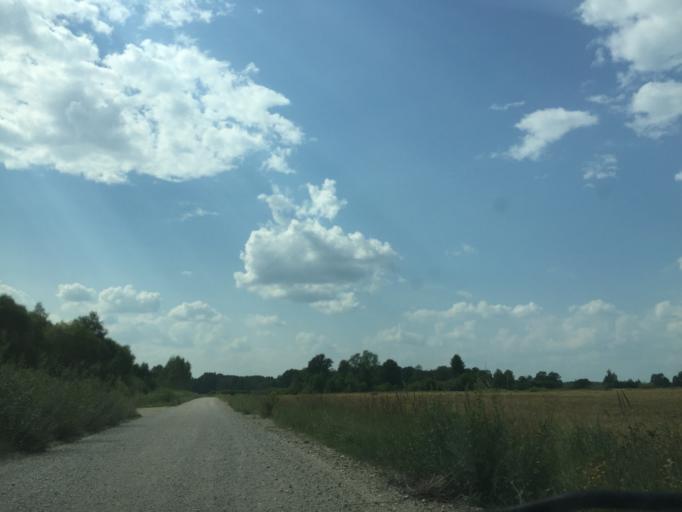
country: LV
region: Auces Novads
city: Auce
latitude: 56.4116
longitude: 23.0223
